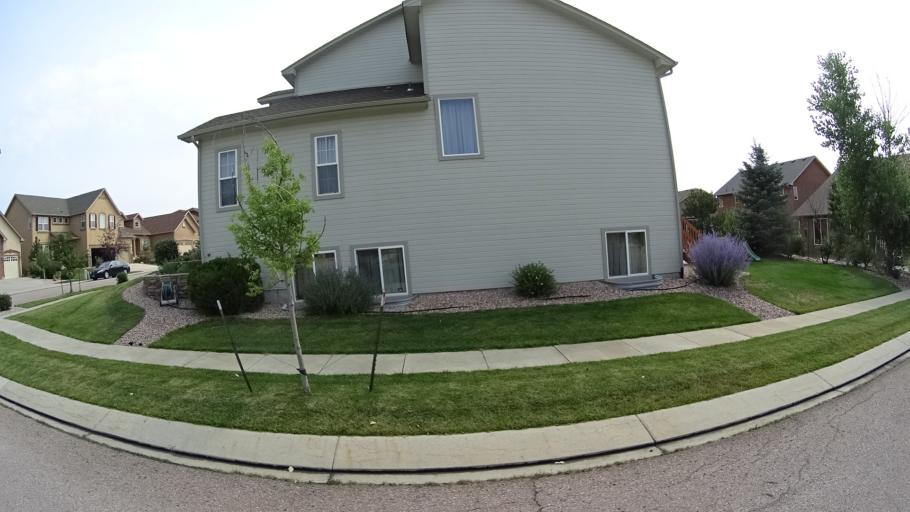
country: US
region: Colorado
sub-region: El Paso County
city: Black Forest
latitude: 38.9629
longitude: -104.7209
